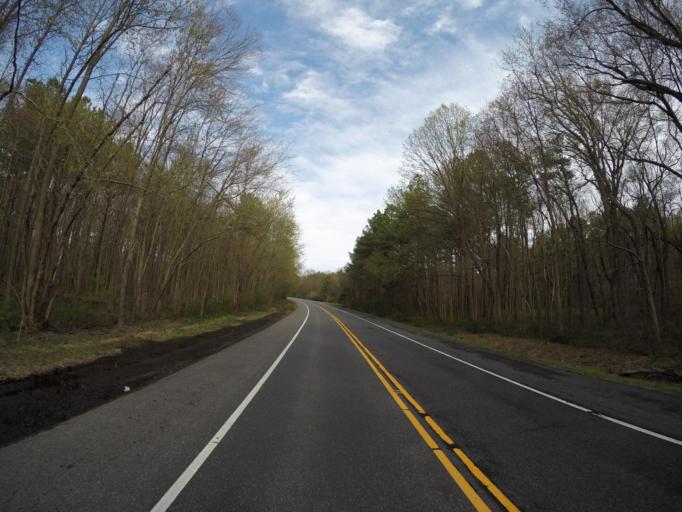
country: US
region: Delaware
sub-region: New Castle County
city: Glasgow
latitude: 39.5474
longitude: -75.7222
